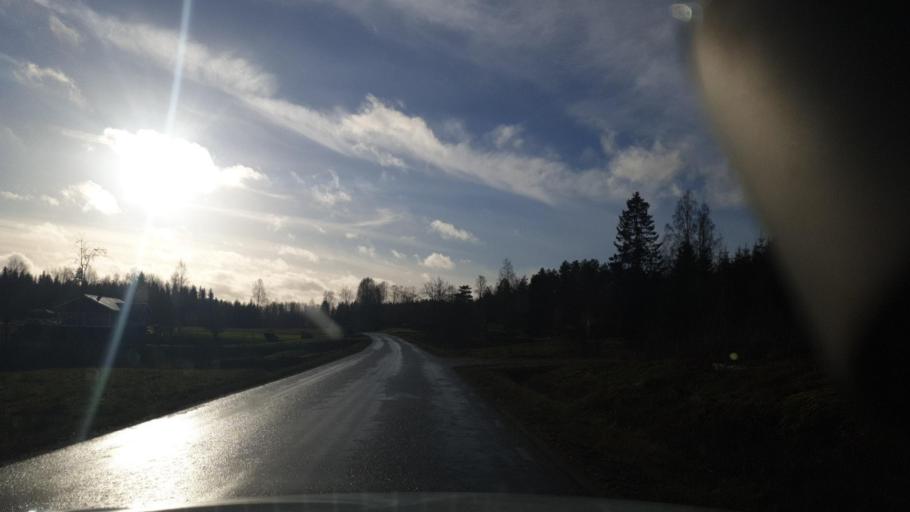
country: SE
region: Vaermland
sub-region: Eda Kommun
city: Charlottenberg
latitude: 59.7960
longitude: 12.1538
